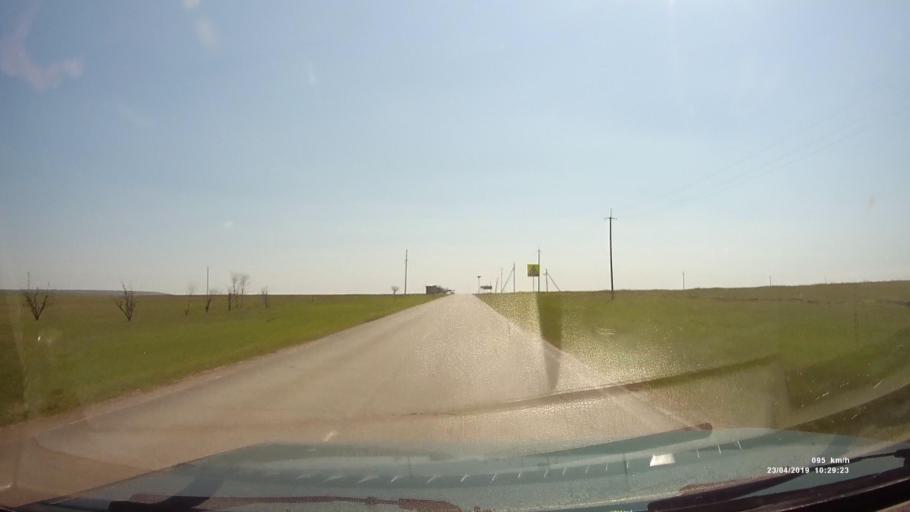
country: RU
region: Kalmykiya
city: Yashalta
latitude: 46.5988
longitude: 42.5256
